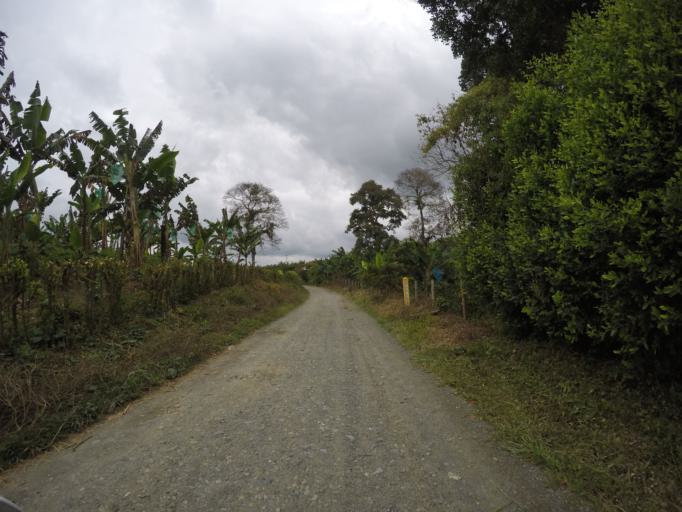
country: CO
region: Quindio
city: Circasia
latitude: 4.6261
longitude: -75.6869
